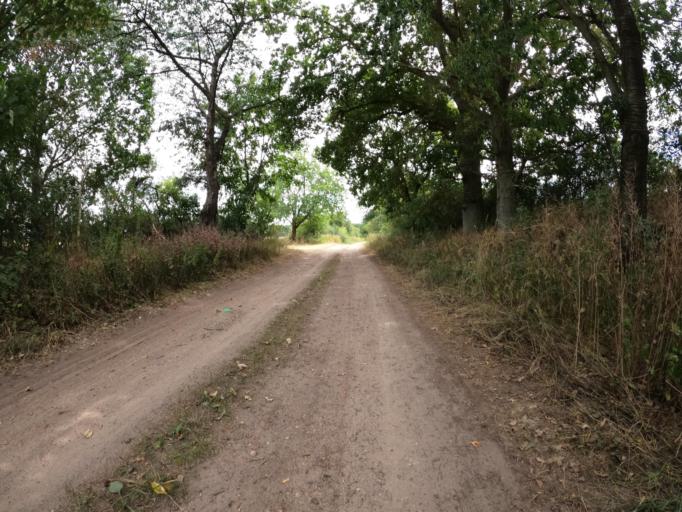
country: DE
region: Mecklenburg-Vorpommern
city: Loitz
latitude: 53.3921
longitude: 13.4442
